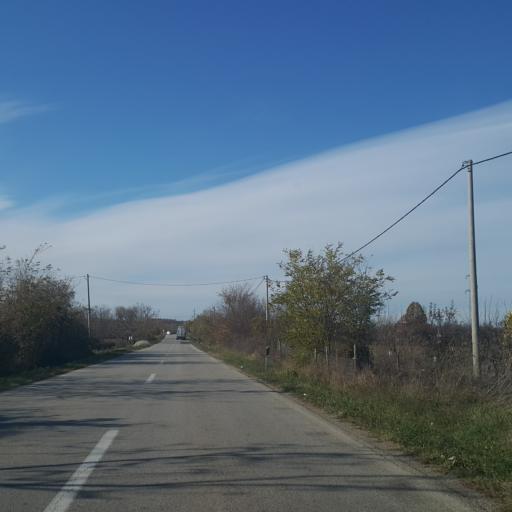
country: RS
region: Central Serbia
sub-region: Sumadijski Okrug
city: Topola
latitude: 44.2513
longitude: 20.7604
